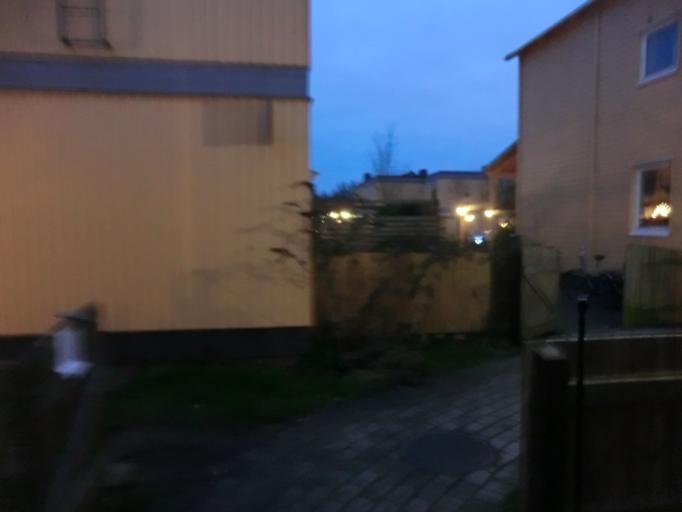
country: SE
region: Skane
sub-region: Lunds Kommun
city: Lund
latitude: 55.7144
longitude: 13.2337
